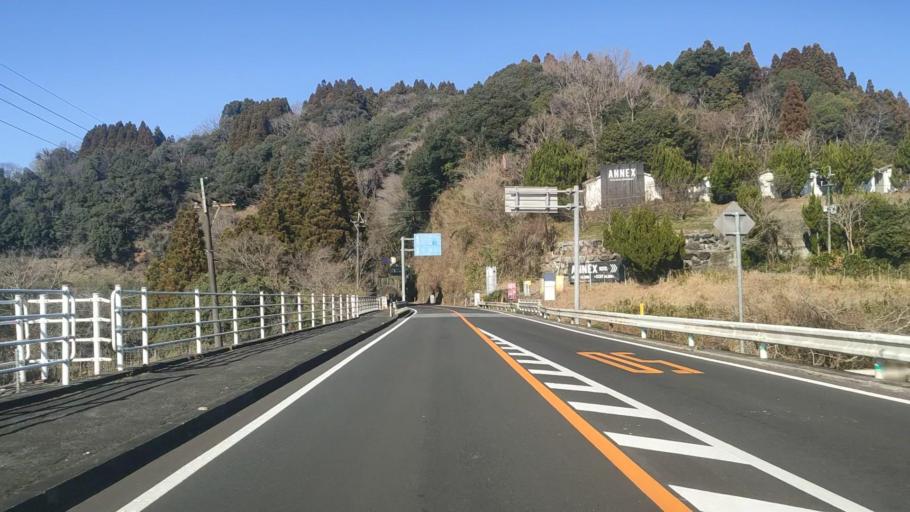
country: JP
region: Oita
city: Usuki
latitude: 33.0531
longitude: 131.6891
